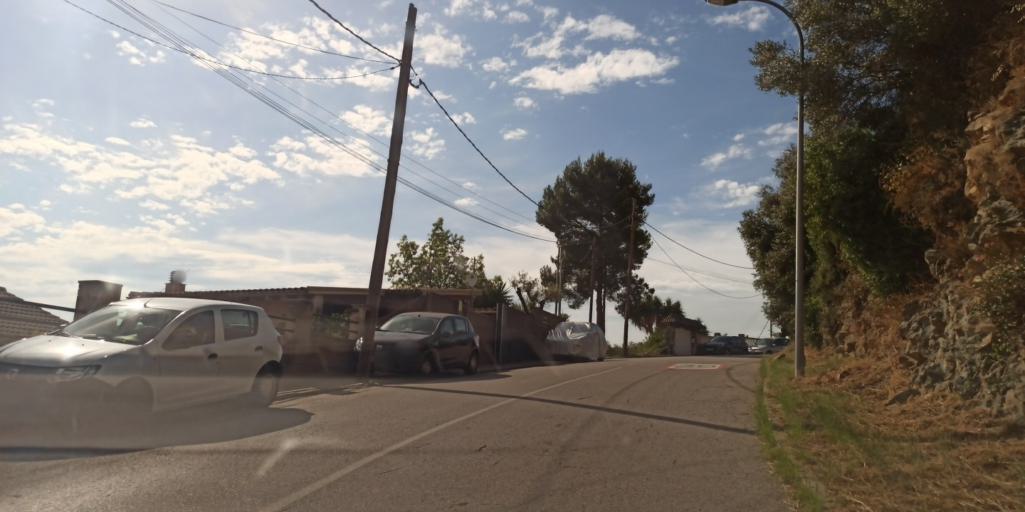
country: ES
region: Catalonia
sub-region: Provincia de Barcelona
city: Torrelles de Llobregat
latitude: 41.3614
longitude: 1.9962
